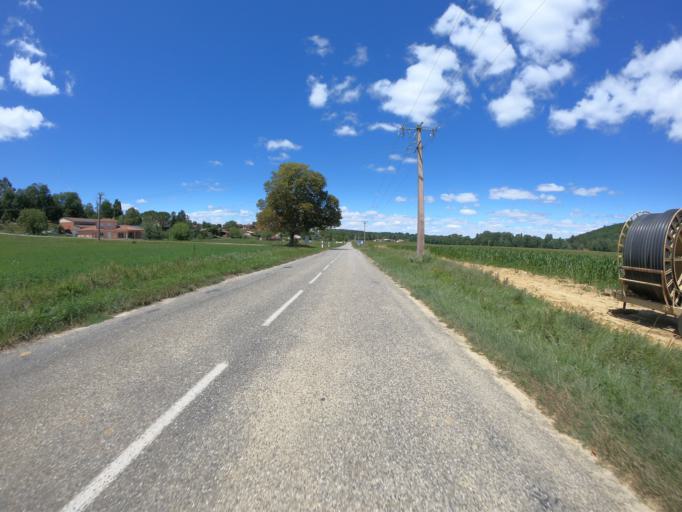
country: FR
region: Midi-Pyrenees
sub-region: Departement de l'Ariege
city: Verniolle
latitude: 43.0601
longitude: 1.7415
